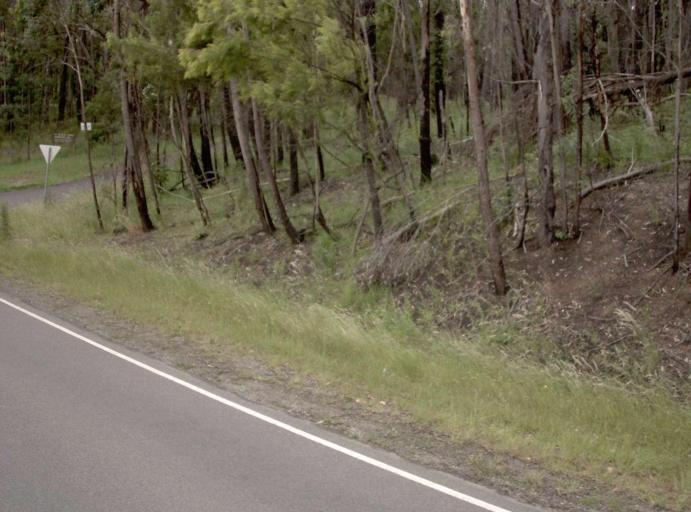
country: AU
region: Victoria
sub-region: Baw Baw
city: Warragul
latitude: -38.0534
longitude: 145.9668
